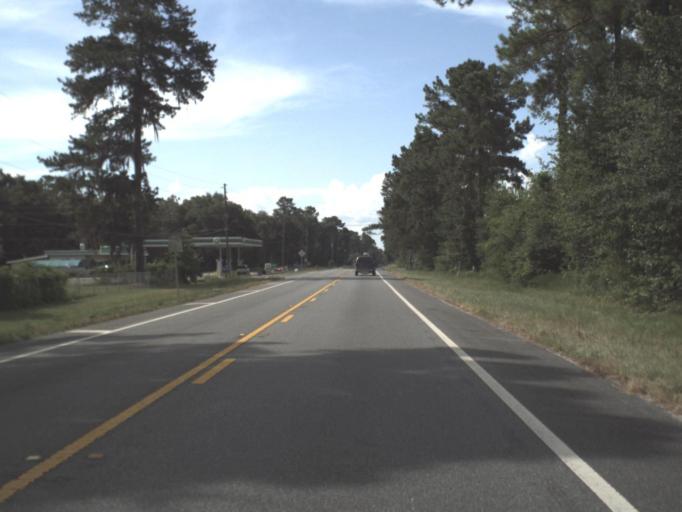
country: US
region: Florida
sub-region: Taylor County
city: Perry
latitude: 30.1639
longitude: -83.5950
